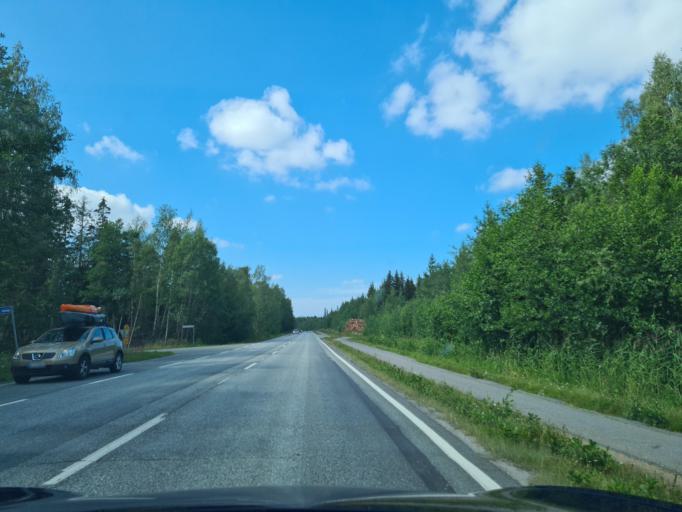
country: FI
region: Ostrobothnia
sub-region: Vaasa
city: Replot
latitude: 63.2006
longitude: 21.5332
